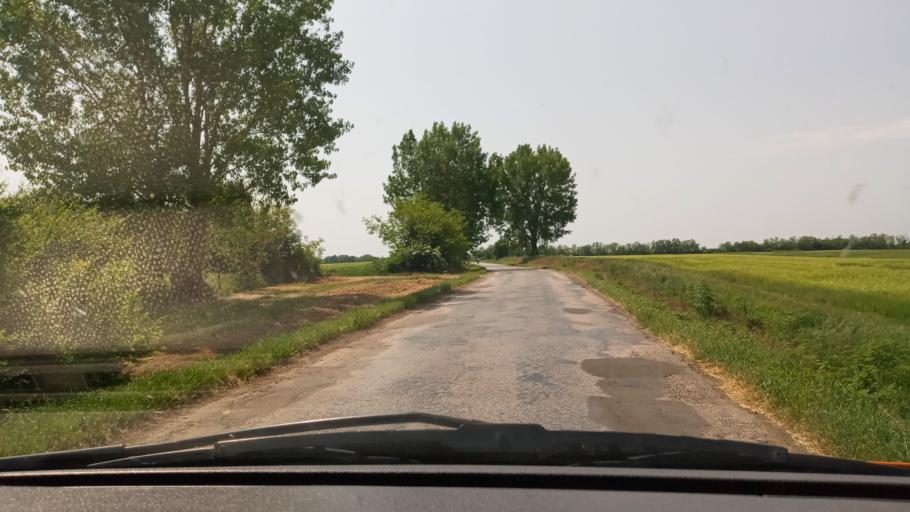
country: HU
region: Baranya
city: Szentlorinc
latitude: 46.0249
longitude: 18.0319
